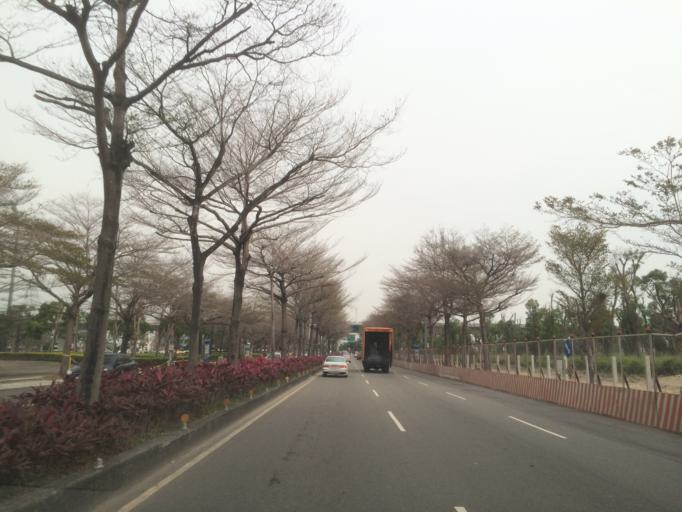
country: TW
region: Taiwan
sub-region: Taichung City
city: Taichung
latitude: 24.1985
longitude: 120.6866
